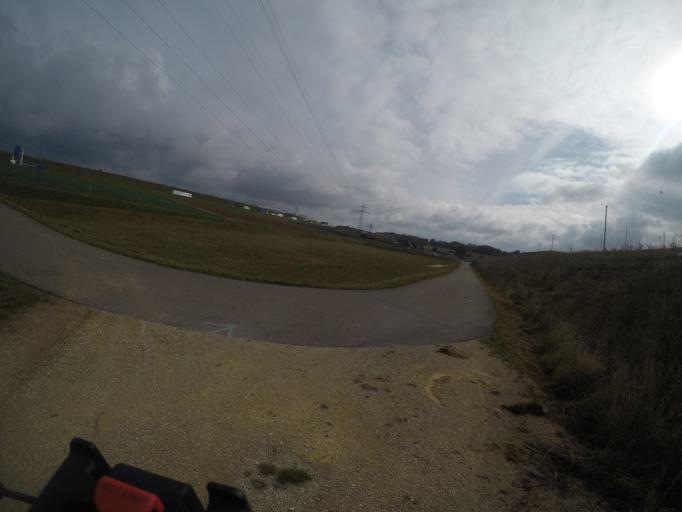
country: DE
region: Baden-Wuerttemberg
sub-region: Tuebingen Region
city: Dornstadt
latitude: 48.4562
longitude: 9.9435
